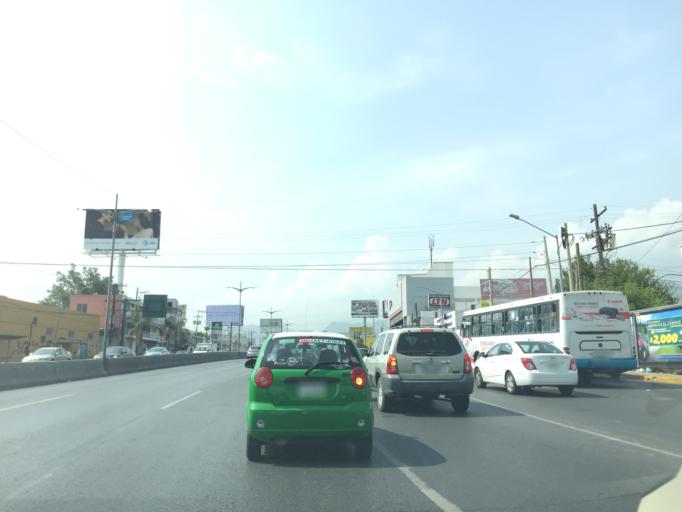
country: MX
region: Nuevo Leon
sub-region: Monterrey
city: Monterrey
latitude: 25.6661
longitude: -100.2974
